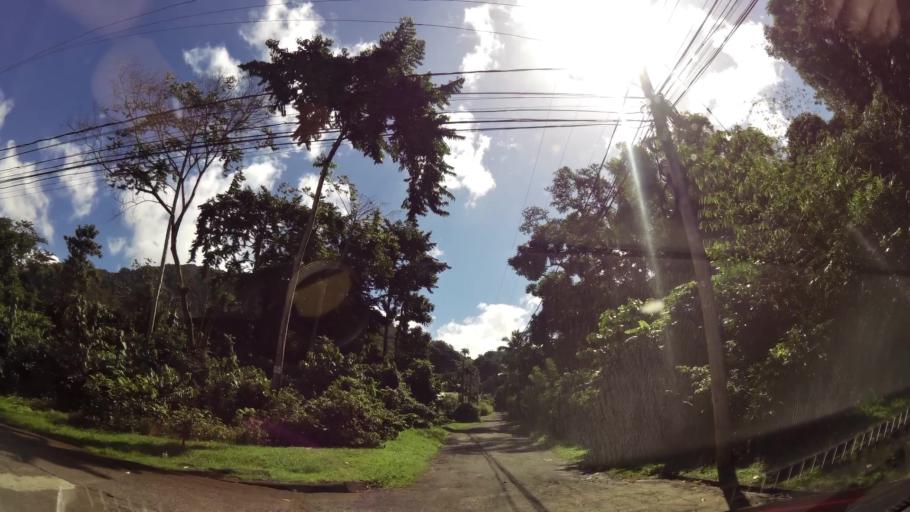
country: DM
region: Saint John
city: Portsmouth
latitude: 15.5578
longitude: -61.4534
